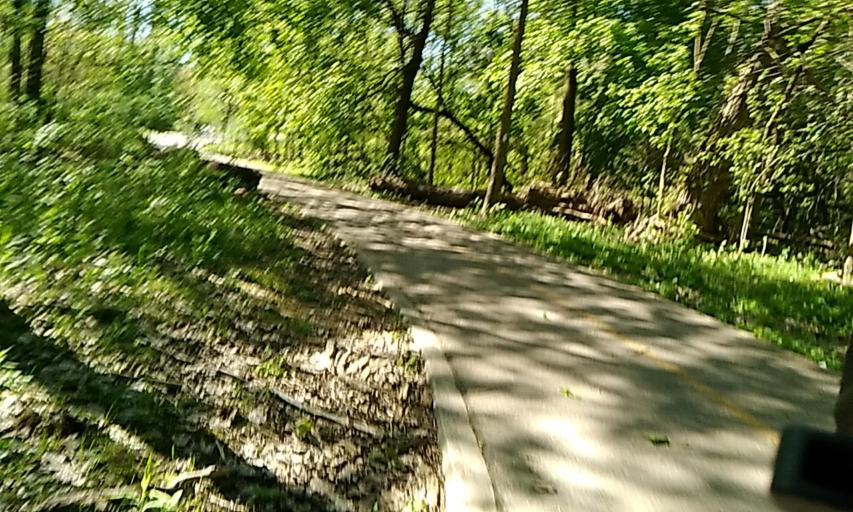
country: CA
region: Ontario
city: London
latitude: 42.9903
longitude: -81.2574
